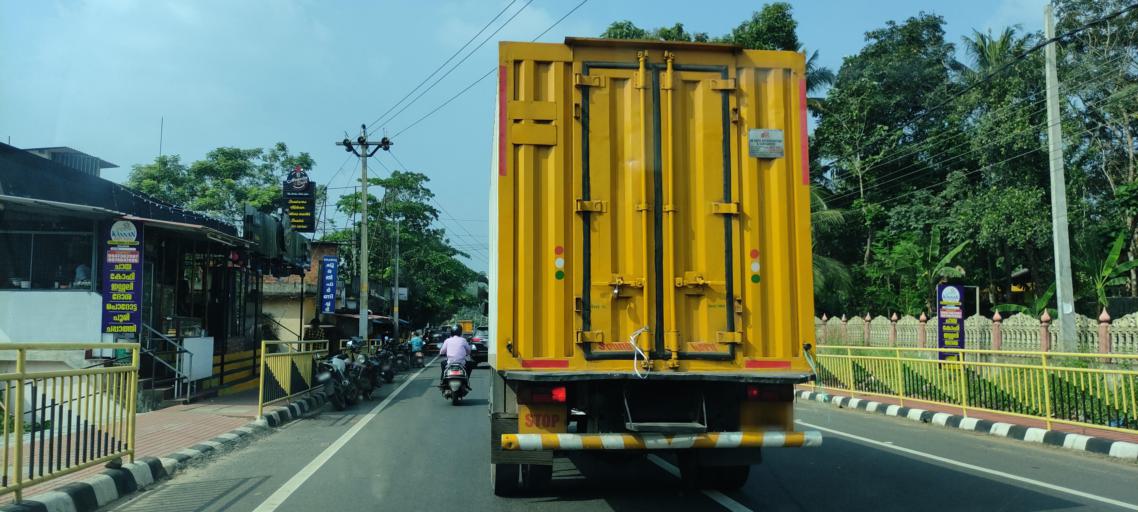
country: IN
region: Kerala
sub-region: Alappuzha
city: Chengannur
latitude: 9.2466
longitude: 76.6690
